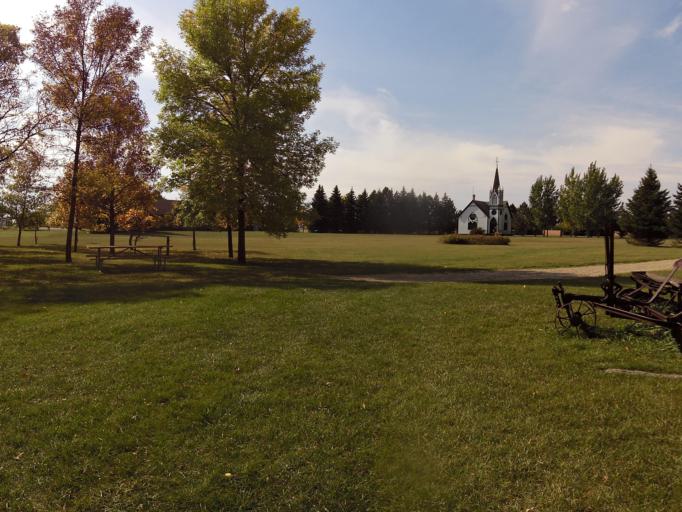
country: US
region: North Dakota
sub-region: Pembina County
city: Cavalier
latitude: 48.7747
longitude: -97.7390
